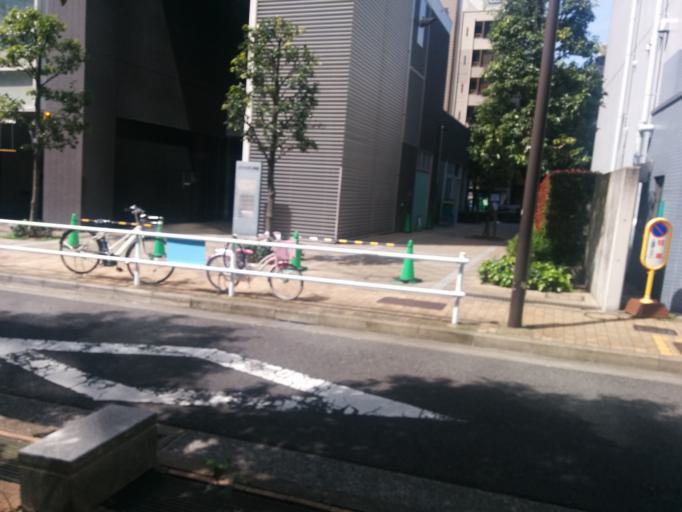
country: JP
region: Tokyo
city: Tokyo
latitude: 35.6948
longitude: 139.6886
